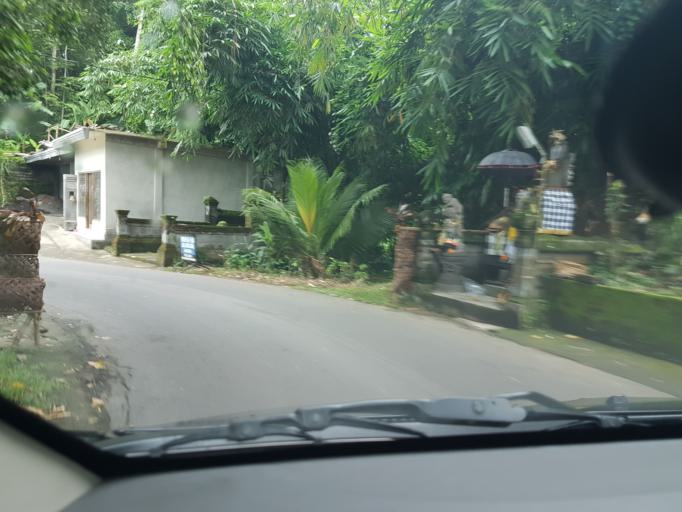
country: ID
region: Bali
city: Banjar Pande
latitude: -8.5035
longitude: 115.2462
